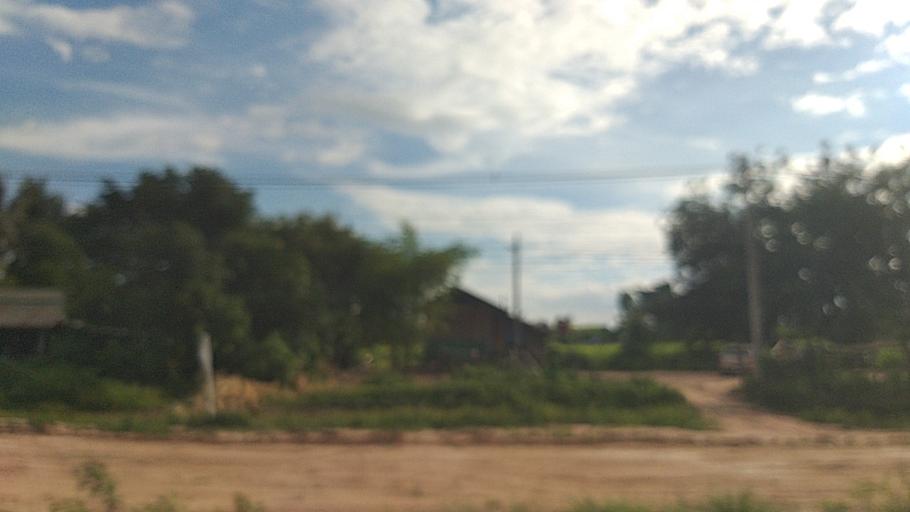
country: TH
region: Surin
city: Kap Choeng
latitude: 14.4906
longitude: 103.5742
